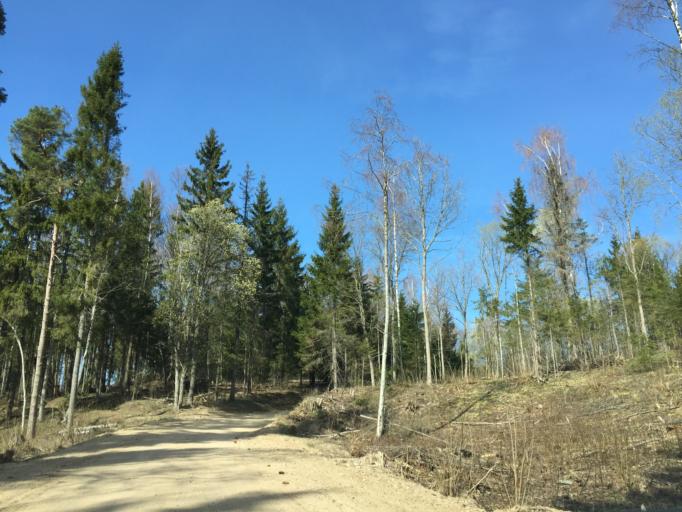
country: EE
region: Vorumaa
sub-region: Antsla vald
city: Vana-Antsla
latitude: 57.9817
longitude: 26.3558
